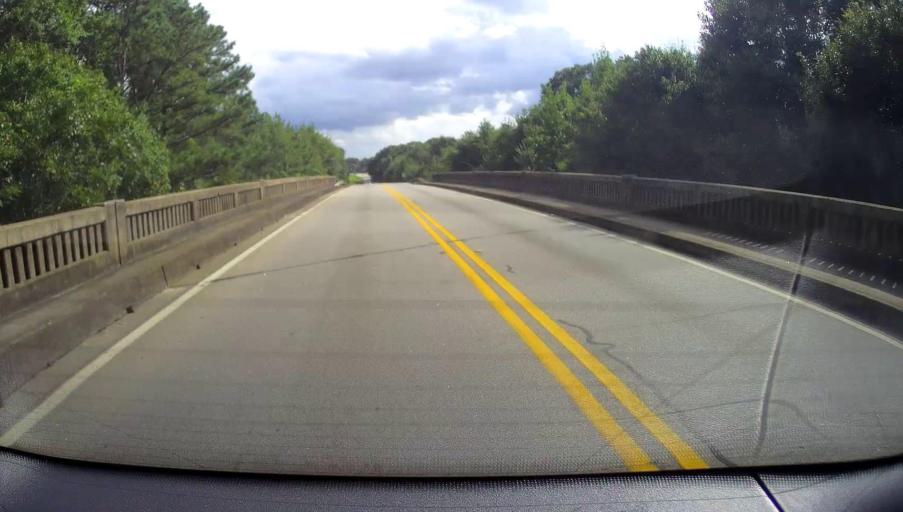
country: US
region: Georgia
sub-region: Meriwether County
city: Manchester
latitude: 32.9825
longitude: -84.5754
